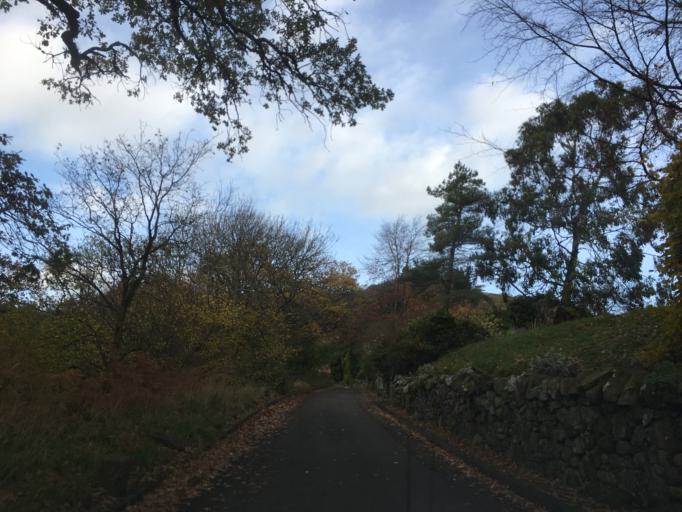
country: GB
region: Scotland
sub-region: Clackmannanshire
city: Dollar
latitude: 56.1702
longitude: -3.6696
